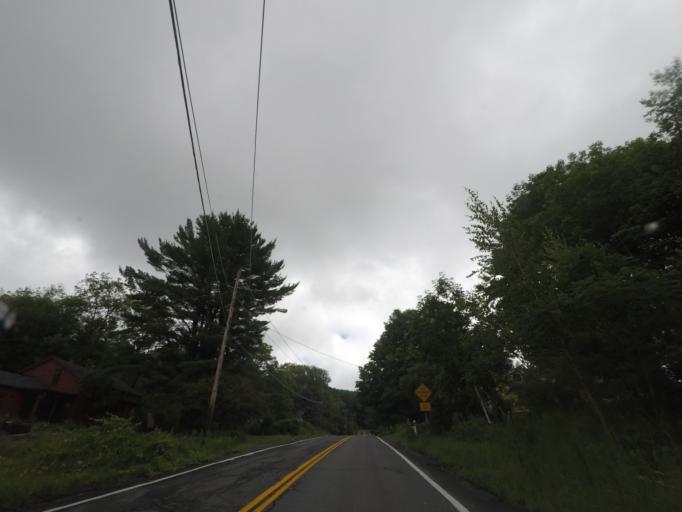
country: US
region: New York
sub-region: Rensselaer County
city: Averill Park
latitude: 42.5803
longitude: -73.4747
